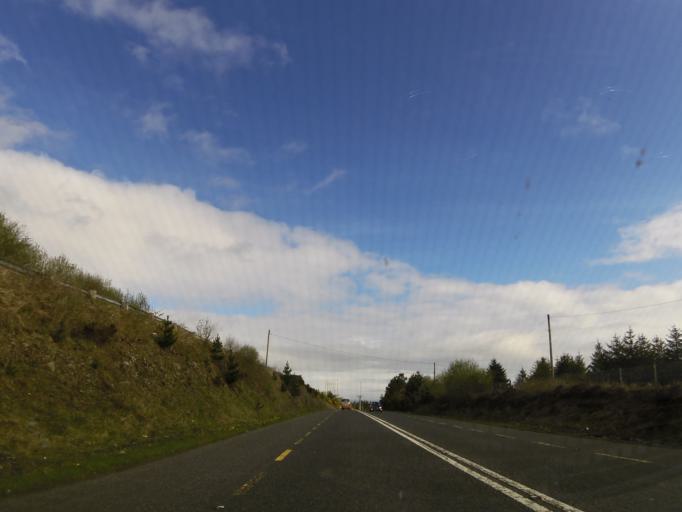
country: IE
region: Connaught
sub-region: Maigh Eo
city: Ballyhaunis
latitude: 53.9096
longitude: -8.7933
